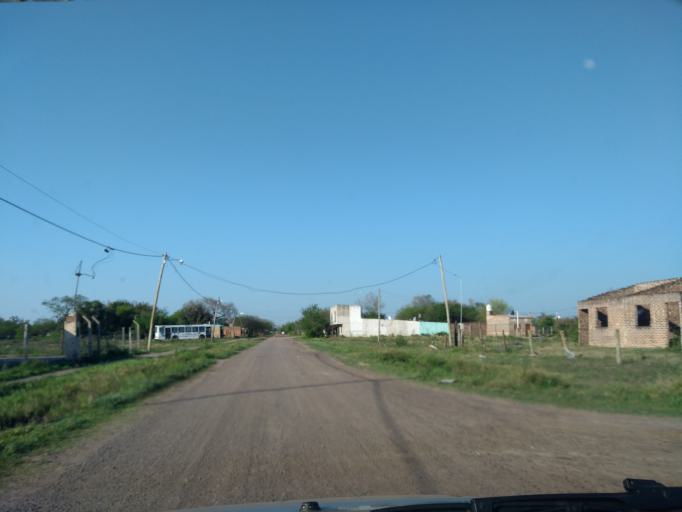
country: AR
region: Chaco
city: Fontana
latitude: -27.4149
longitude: -59.0580
